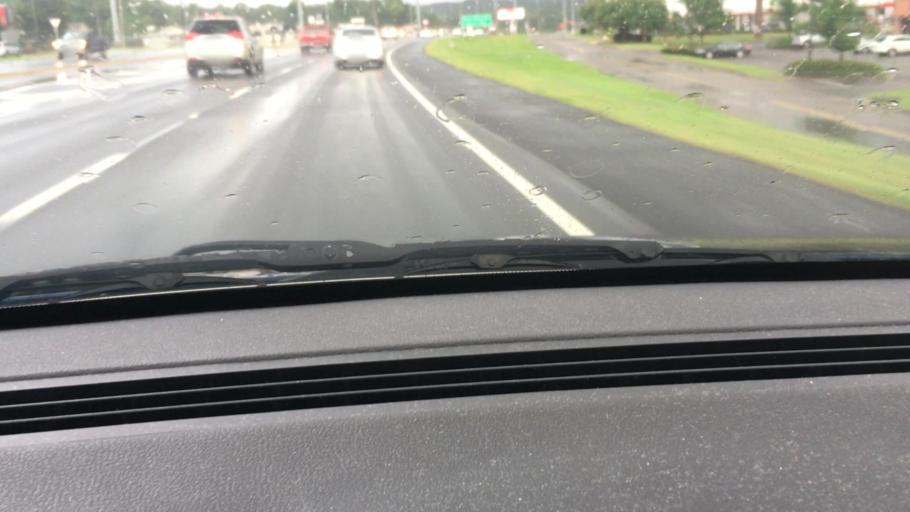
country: US
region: Alabama
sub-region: Tuscaloosa County
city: Tuscaloosa
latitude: 33.2324
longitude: -87.5378
